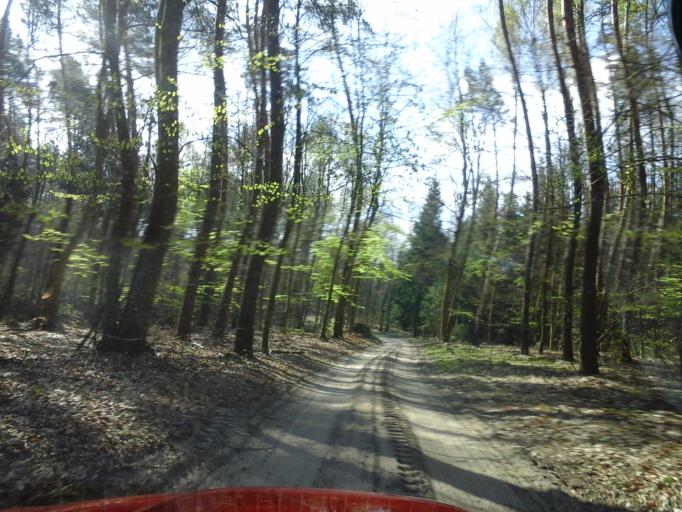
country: PL
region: West Pomeranian Voivodeship
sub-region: Powiat choszczenski
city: Bierzwnik
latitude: 53.0137
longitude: 15.6142
